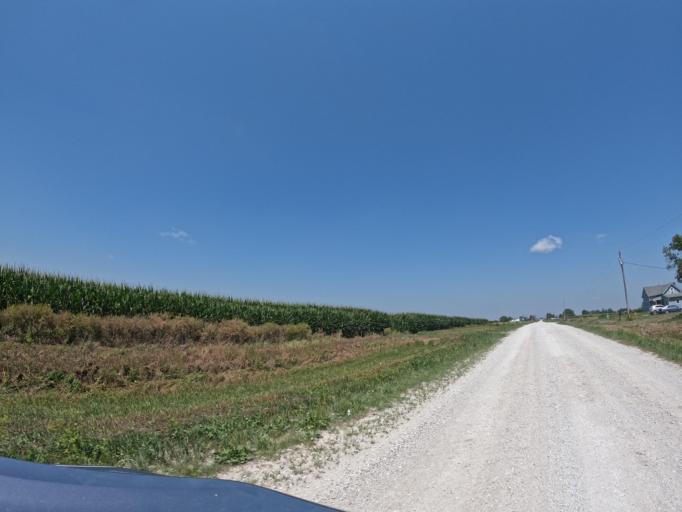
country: US
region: Iowa
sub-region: Keokuk County
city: Sigourney
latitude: 41.2643
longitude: -92.1700
